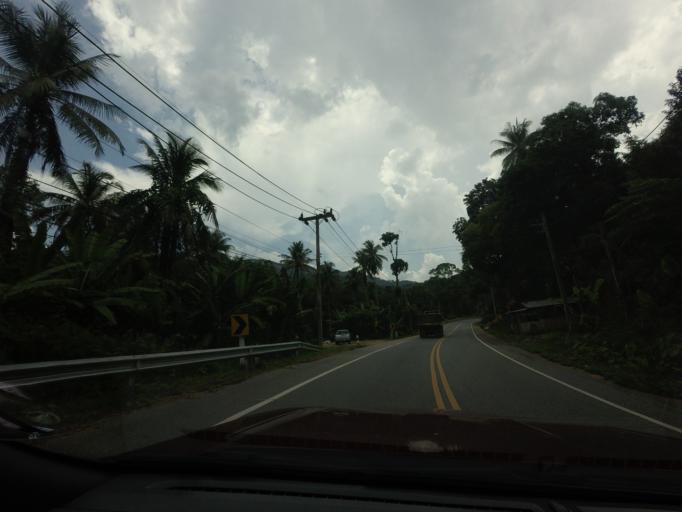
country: TH
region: Yala
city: Than To
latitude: 6.0838
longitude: 101.1822
